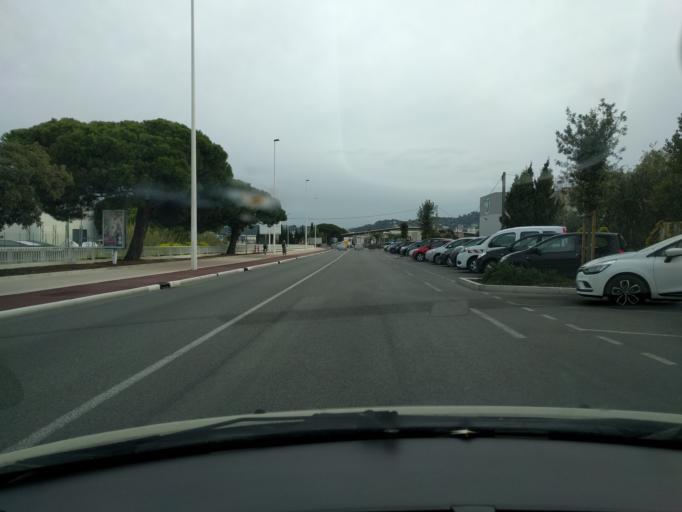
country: FR
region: Provence-Alpes-Cote d'Azur
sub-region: Departement des Alpes-Maritimes
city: Mandelieu-la-Napoule
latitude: 43.5443
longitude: 6.9607
